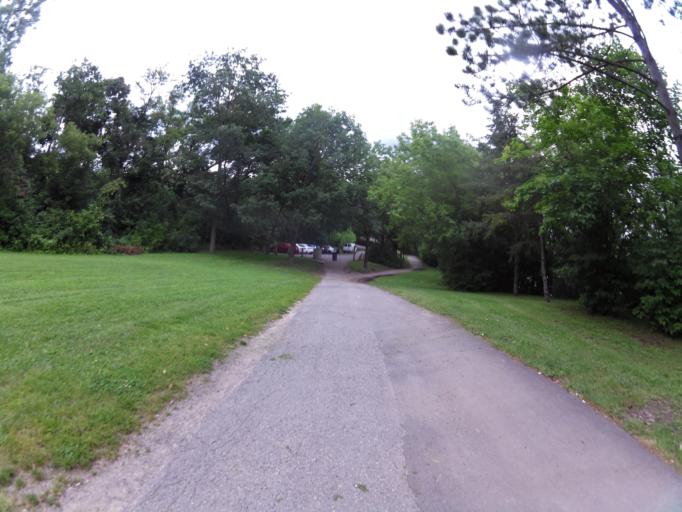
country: CA
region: Ontario
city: Ottawa
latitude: 45.4215
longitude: -75.6683
